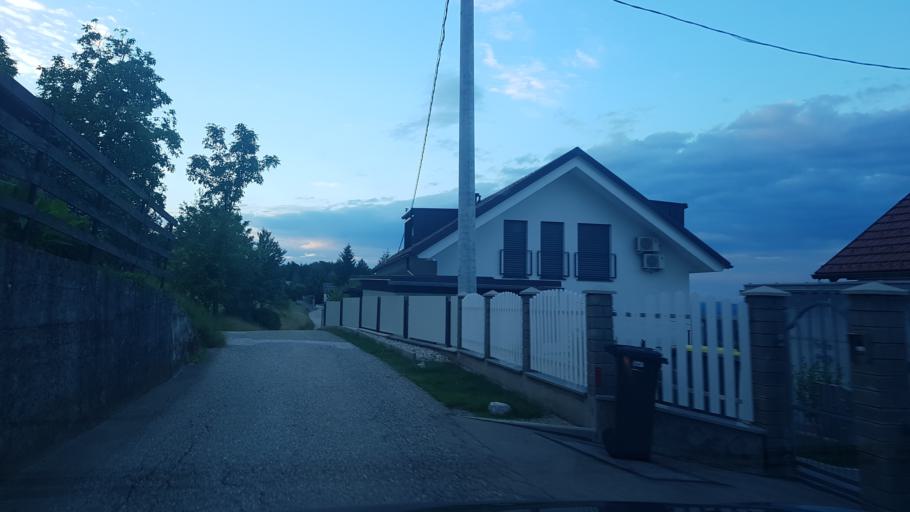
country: SI
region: Grosuplje
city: Smarje-Sap
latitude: 45.9209
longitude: 14.5891
